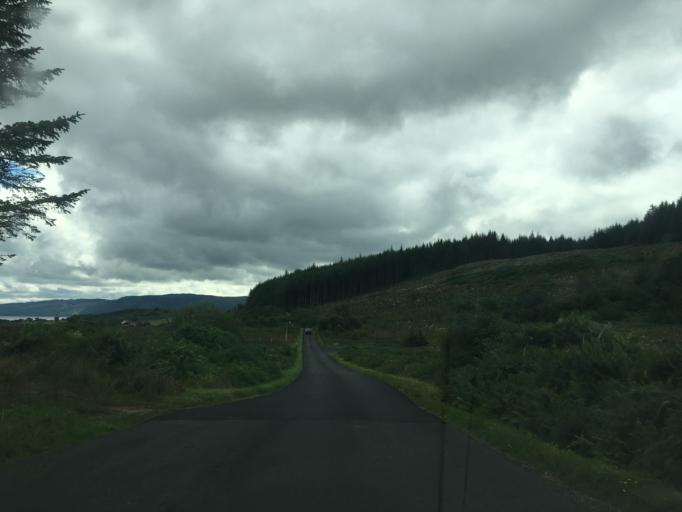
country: GB
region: Scotland
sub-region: Argyll and Bute
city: Tarbert
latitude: 55.8757
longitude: -5.2813
